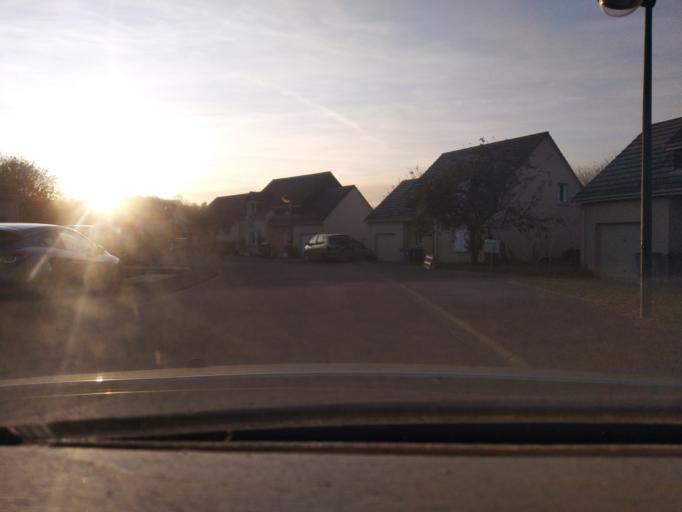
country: FR
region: Haute-Normandie
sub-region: Departement de la Seine-Maritime
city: Yainville
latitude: 49.4534
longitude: 0.8285
